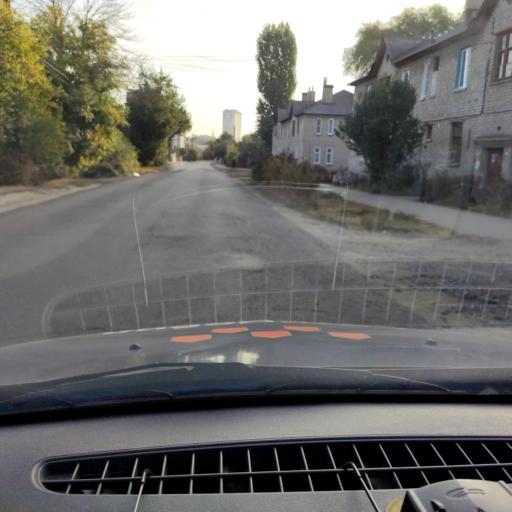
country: RU
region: Voronezj
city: Voronezh
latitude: 51.6922
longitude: 39.1722
